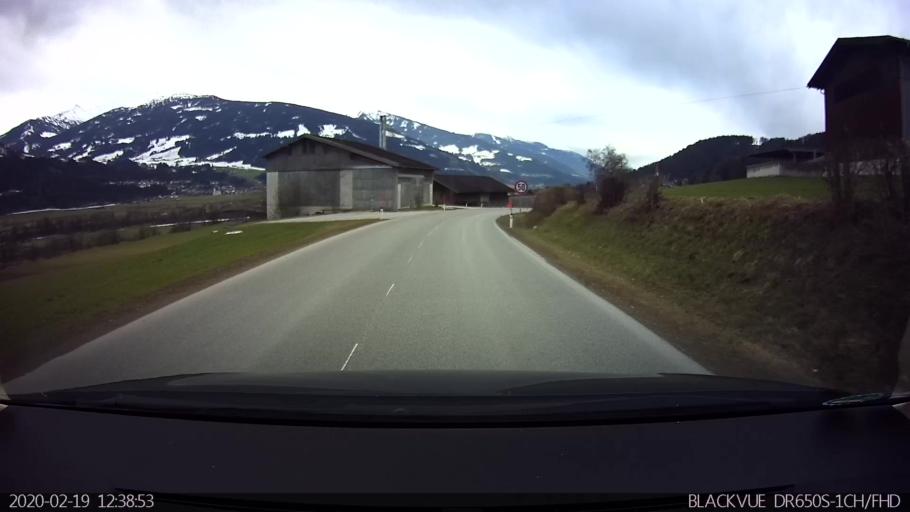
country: AT
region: Tyrol
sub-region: Politischer Bezirk Schwaz
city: Terfens
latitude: 47.3252
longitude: 11.6483
